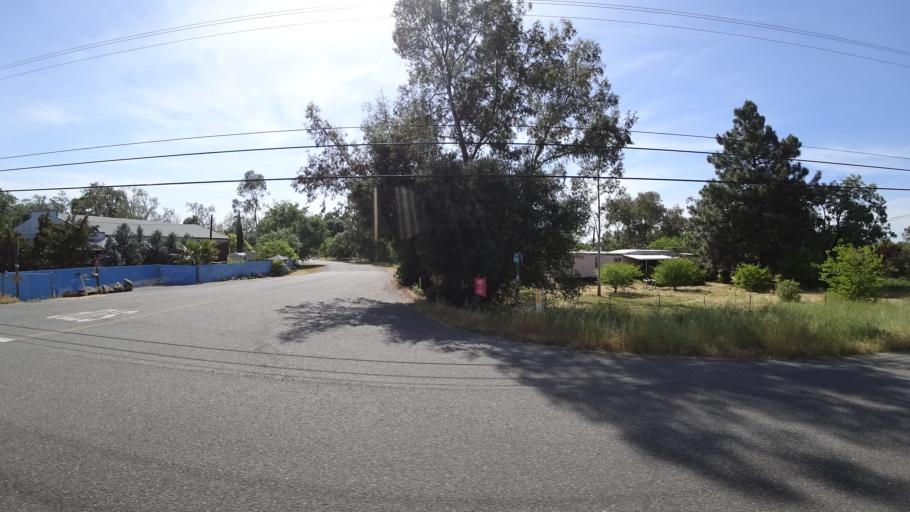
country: US
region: California
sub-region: Tehama County
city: Los Molinos
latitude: 40.0445
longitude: -122.1003
